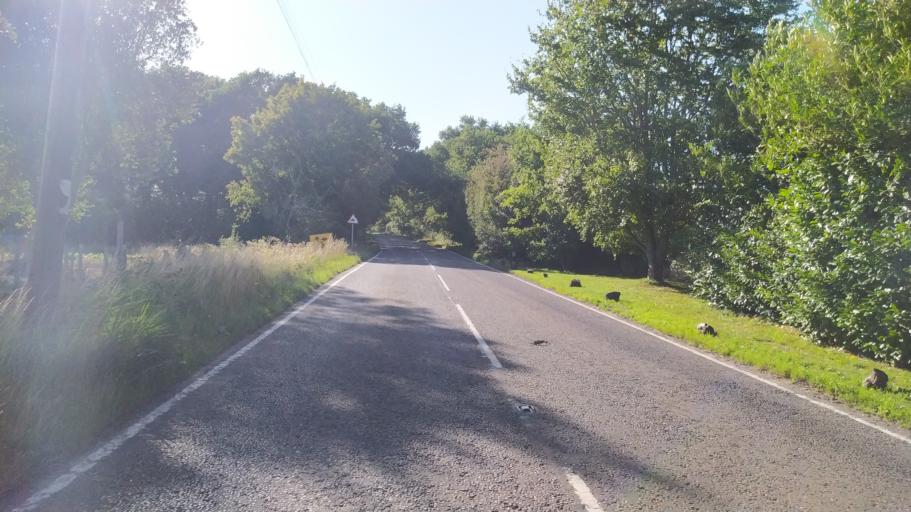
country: GB
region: England
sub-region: Hampshire
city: Kingsley
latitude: 51.1354
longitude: -0.9023
